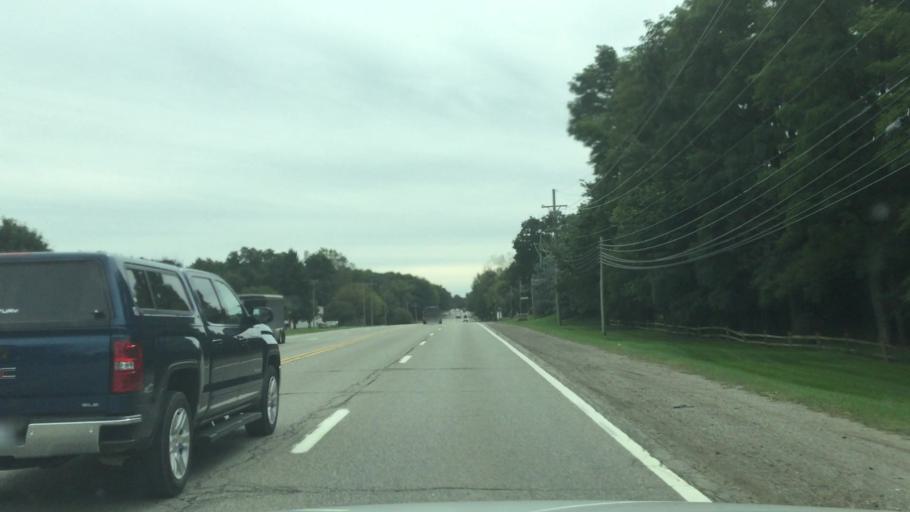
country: US
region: Michigan
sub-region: Oakland County
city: Clarkston
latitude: 42.7719
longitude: -83.4912
